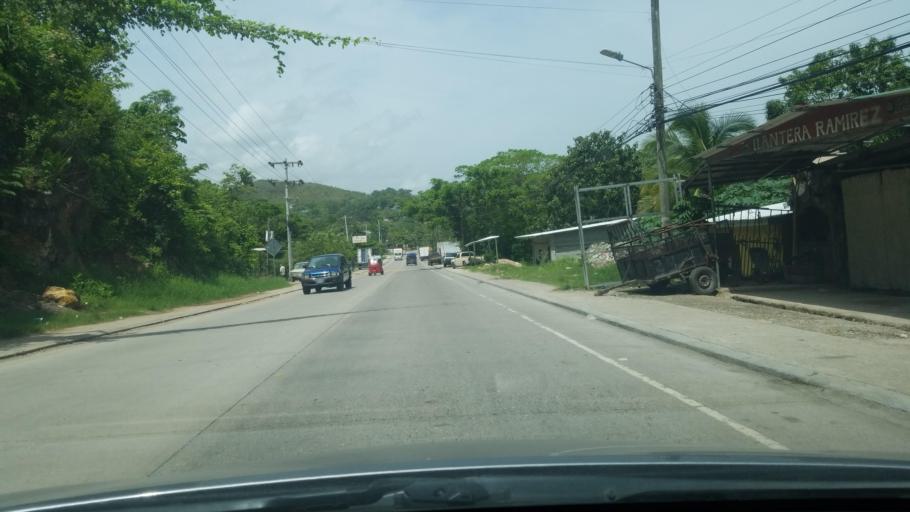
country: HN
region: Copan
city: La Entrada
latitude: 15.0509
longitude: -88.7556
